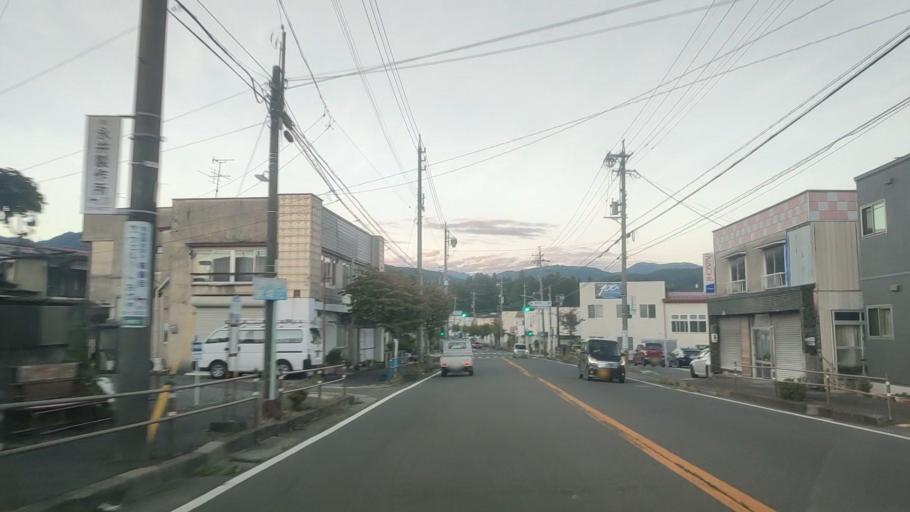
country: JP
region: Nagano
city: Okaya
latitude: 36.0735
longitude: 138.0619
